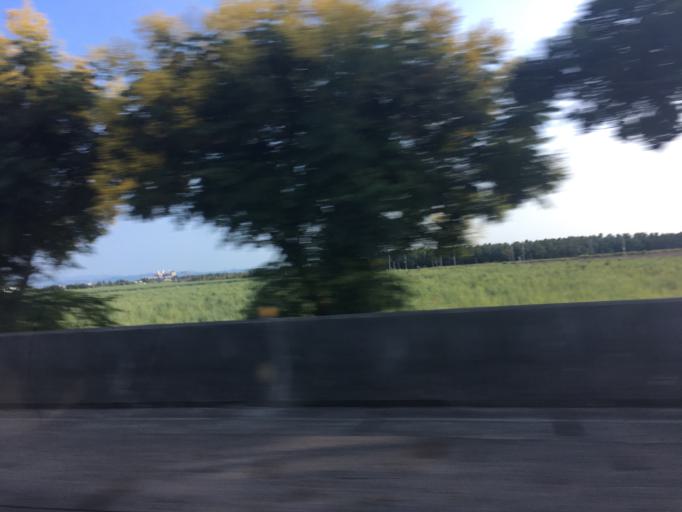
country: TW
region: Taiwan
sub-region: Chiayi
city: Taibao
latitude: 23.4264
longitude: 120.3482
